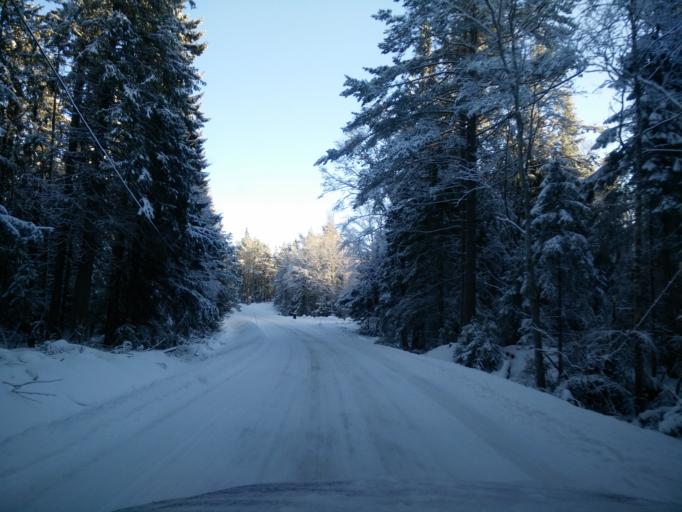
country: SE
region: Vaesternorrland
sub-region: Sundsvalls Kommun
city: Njurundabommen
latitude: 62.2329
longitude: 17.6322
